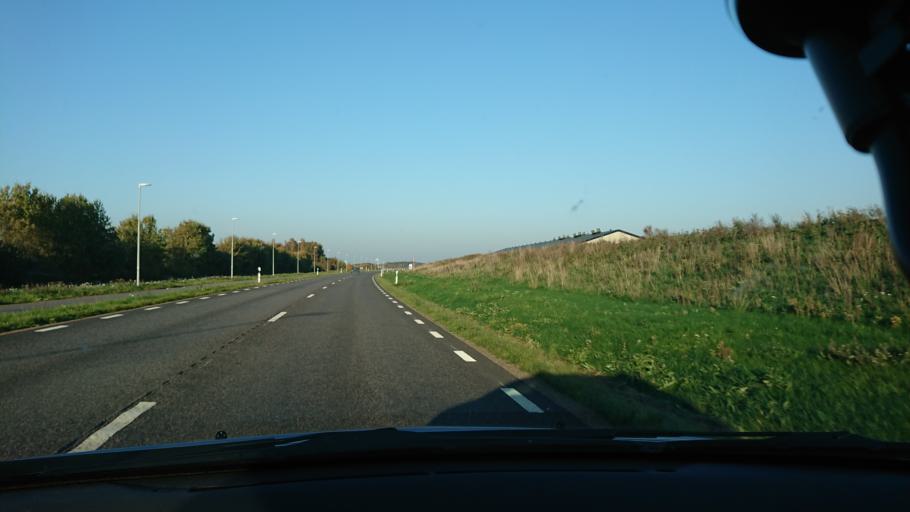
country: SE
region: Skane
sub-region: Bastads Kommun
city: Bastad
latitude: 56.4400
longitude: 12.9214
